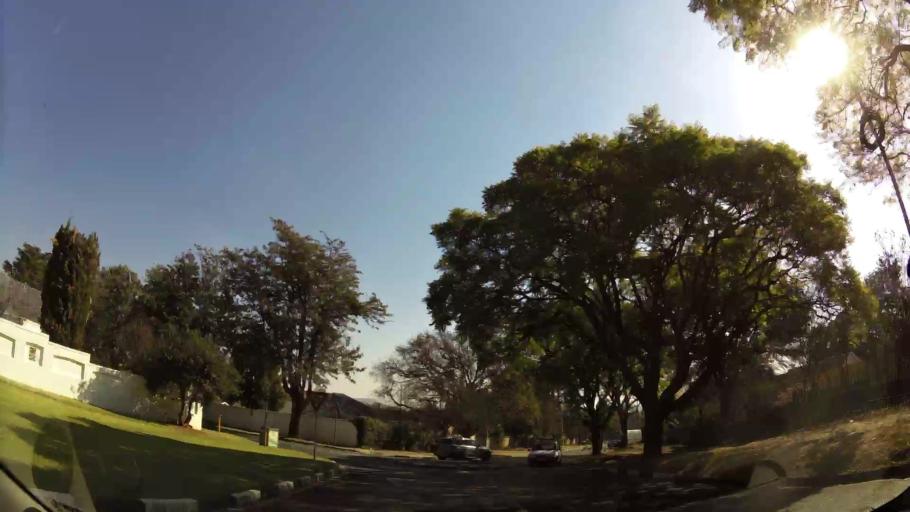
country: ZA
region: Gauteng
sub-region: City of Johannesburg Metropolitan Municipality
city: Johannesburg
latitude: -26.1370
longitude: 28.0321
